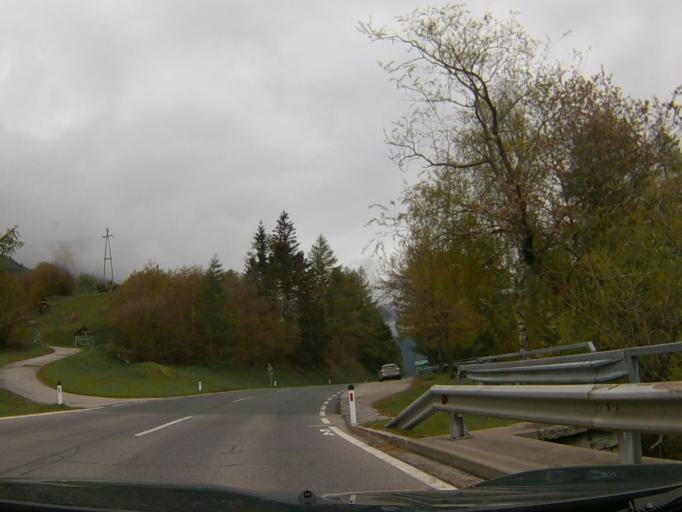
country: AT
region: Carinthia
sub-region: Politischer Bezirk Spittal an der Drau
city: Obervellach
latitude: 46.9711
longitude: 13.1820
